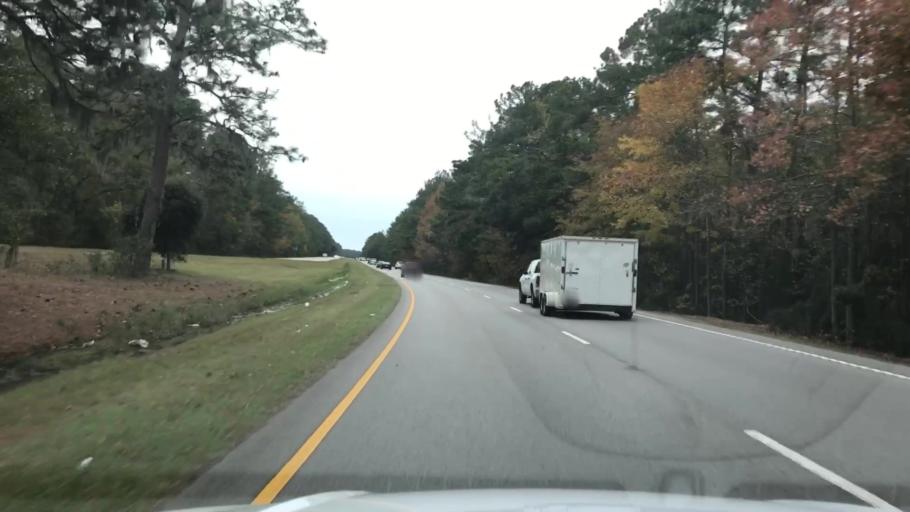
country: US
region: South Carolina
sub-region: Georgetown County
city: Georgetown
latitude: 33.4033
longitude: -79.1999
